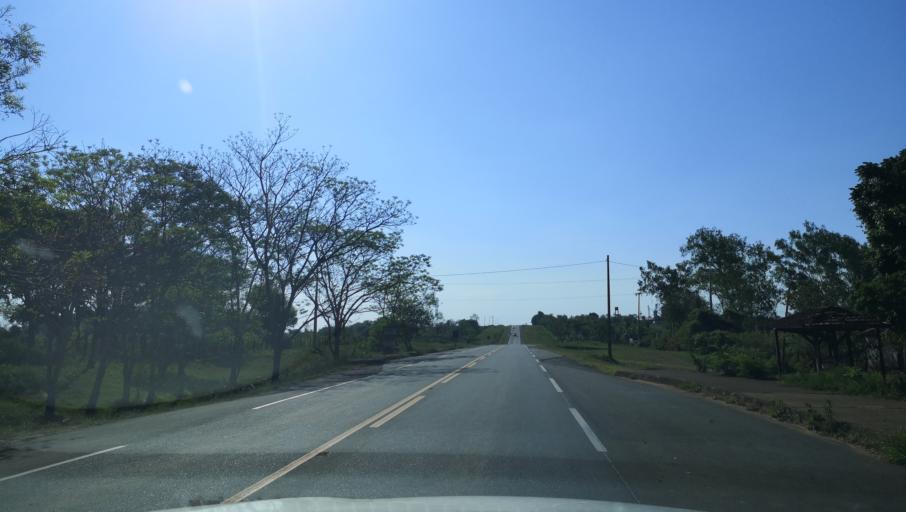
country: PY
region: Misiones
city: Santa Rosa
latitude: -26.8874
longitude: -56.9440
